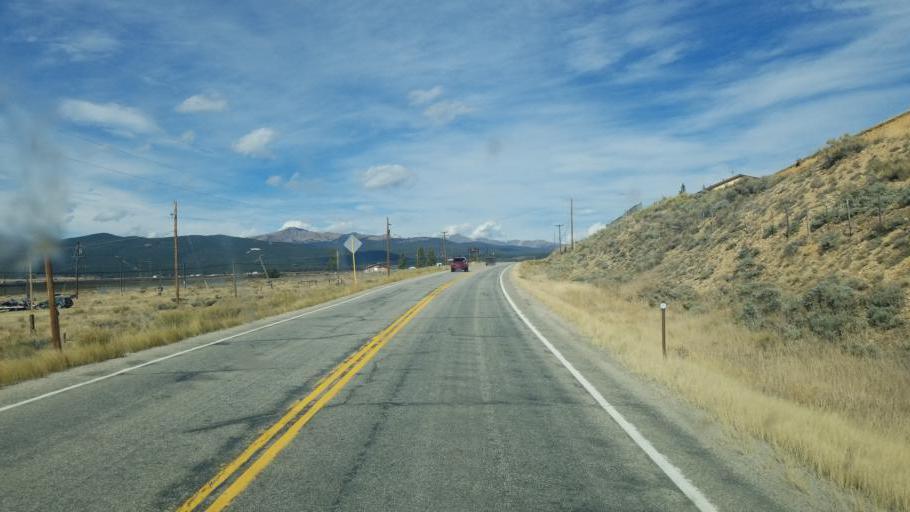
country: US
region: Colorado
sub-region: Lake County
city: Leadville North
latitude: 39.2043
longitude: -106.3442
